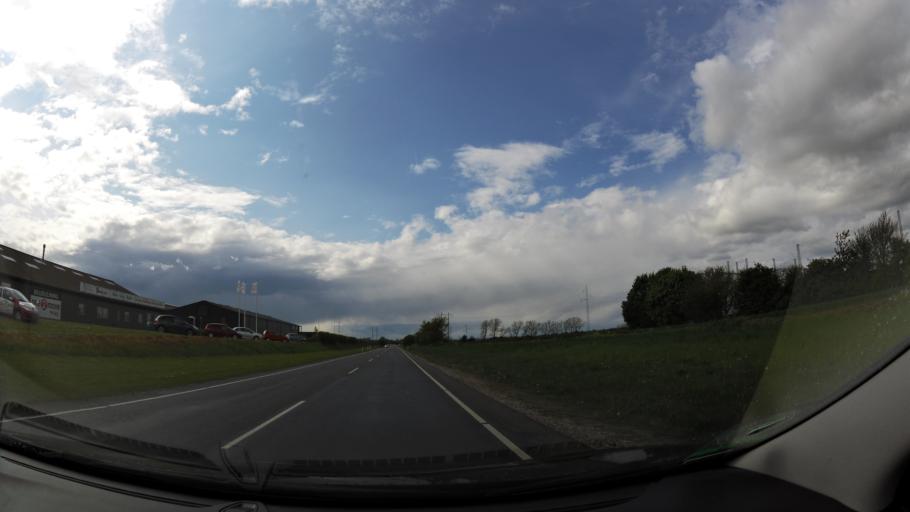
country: DK
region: South Denmark
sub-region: Nyborg Kommune
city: Nyborg
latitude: 55.3166
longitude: 10.7522
